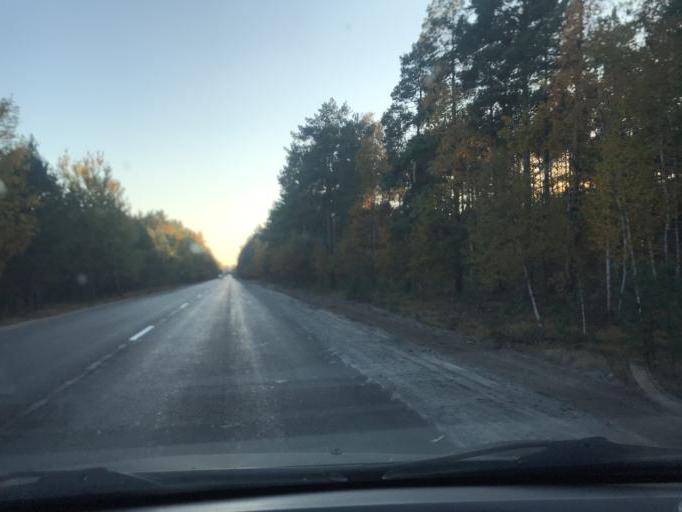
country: BY
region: Gomel
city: Brahin
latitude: 51.8685
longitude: 30.3776
